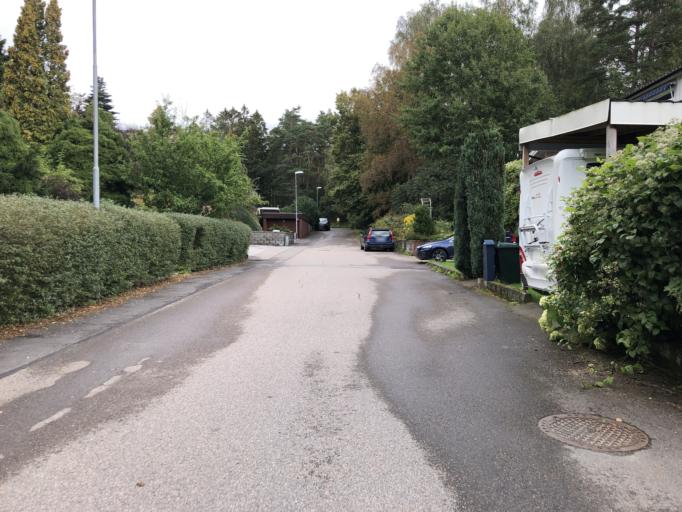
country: SE
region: Vaestra Goetaland
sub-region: Goteborg
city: Majorna
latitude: 57.7432
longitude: 11.9040
